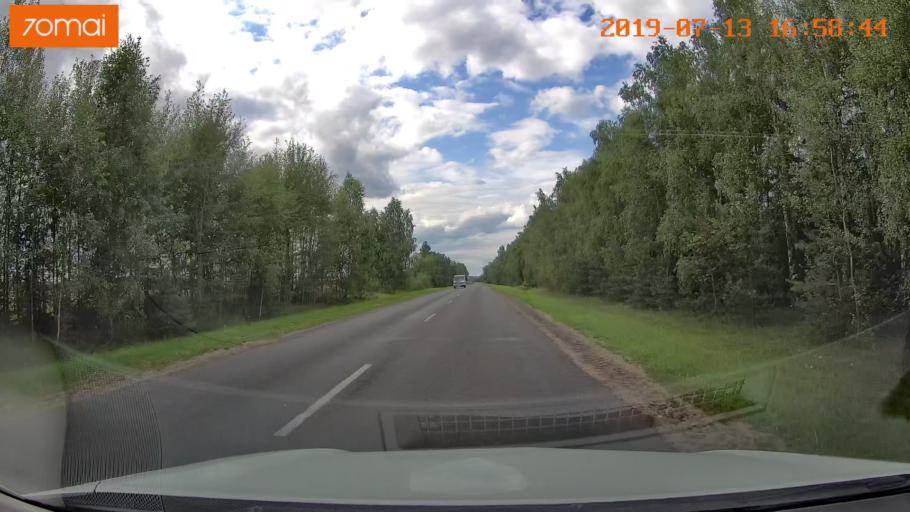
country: BY
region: Mogilev
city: Kirawsk
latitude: 53.2919
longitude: 29.4393
